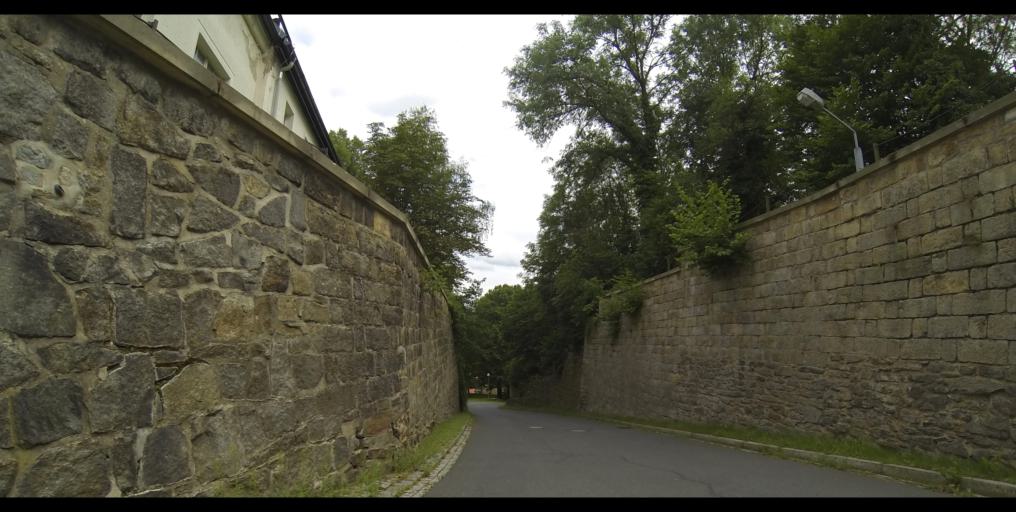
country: DE
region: Saxony
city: Grossschirma
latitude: 50.9998
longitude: 13.3058
